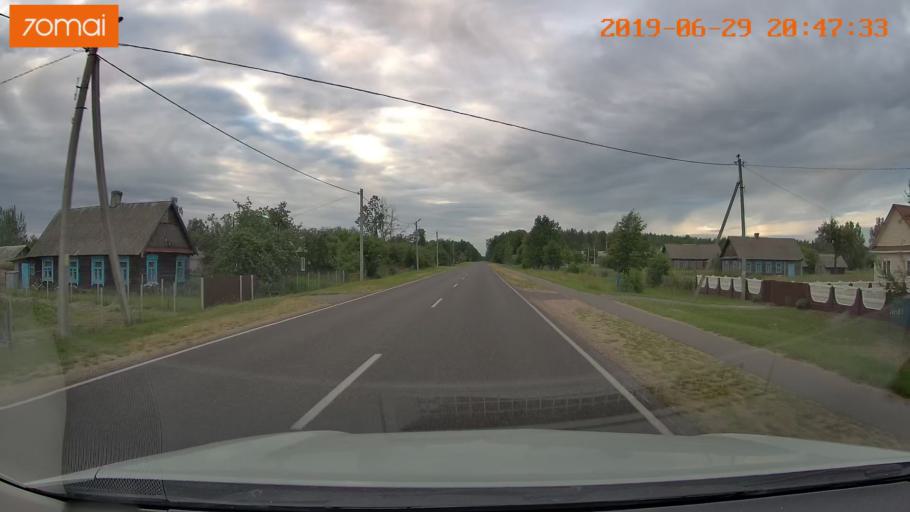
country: BY
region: Brest
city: Hantsavichy
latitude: 52.6398
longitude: 26.3158
